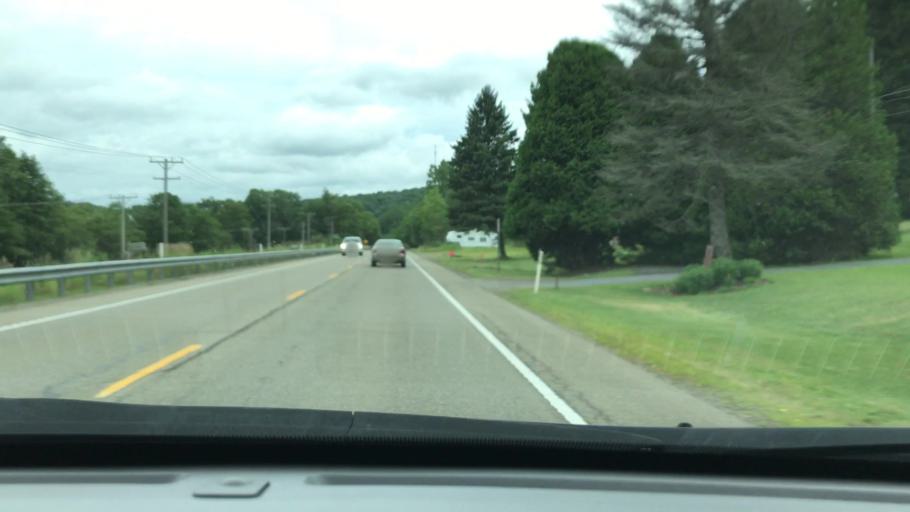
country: US
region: Pennsylvania
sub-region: Elk County
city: Johnsonburg
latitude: 41.5512
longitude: -78.6829
